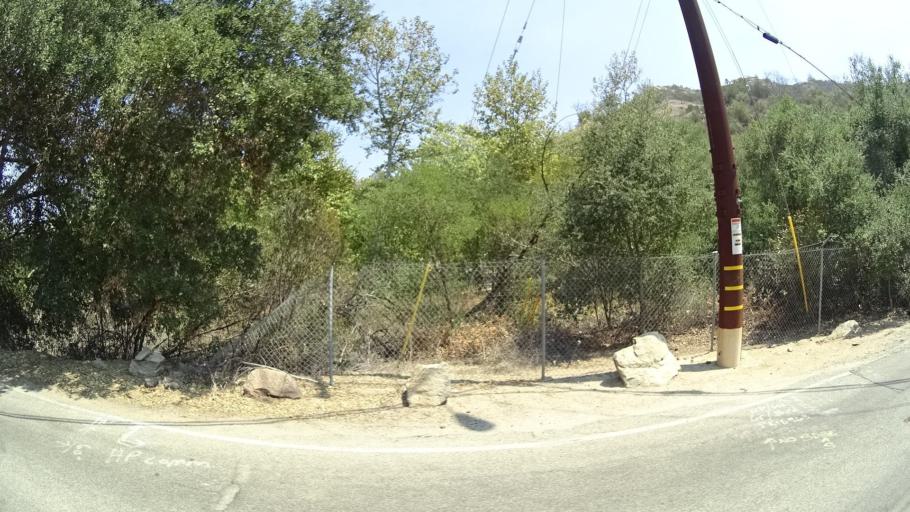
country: US
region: California
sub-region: San Diego County
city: Fallbrook
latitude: 33.4347
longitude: -117.3013
